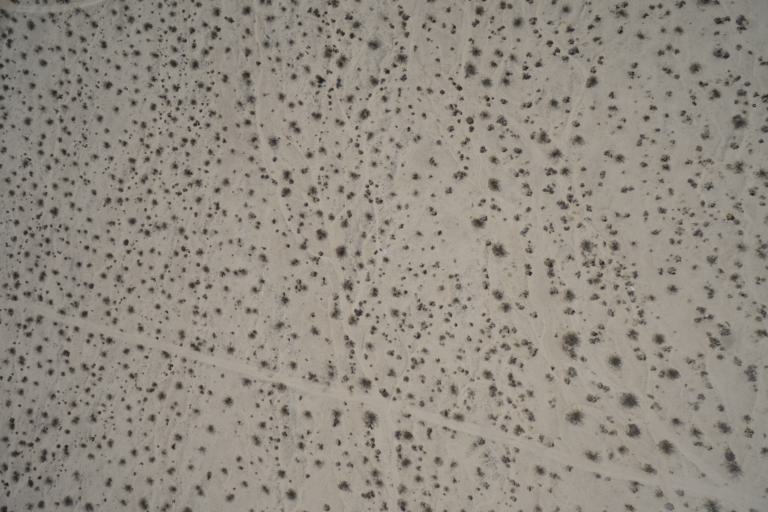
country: US
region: California
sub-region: San Bernardino County
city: Twentynine Palms
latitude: 34.1264
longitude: -116.0254
